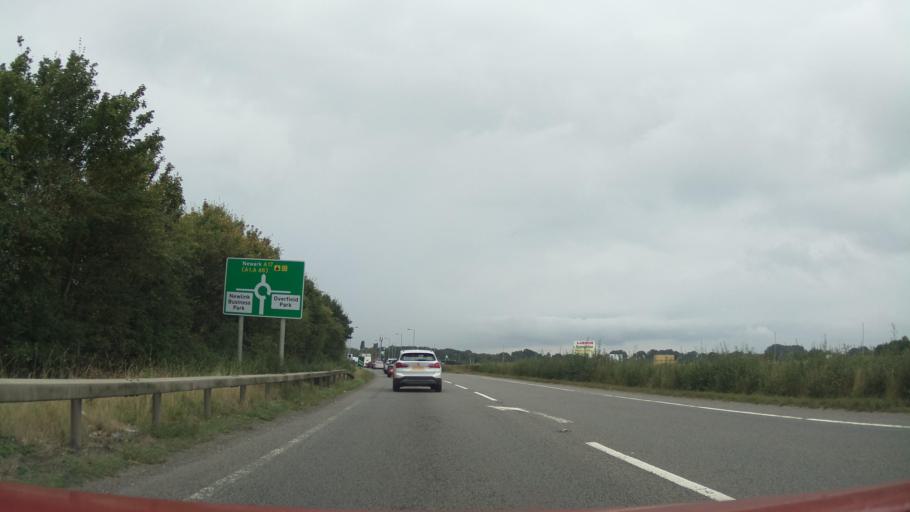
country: GB
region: England
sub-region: Nottinghamshire
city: South Collingham
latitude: 53.0941
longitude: -0.7752
